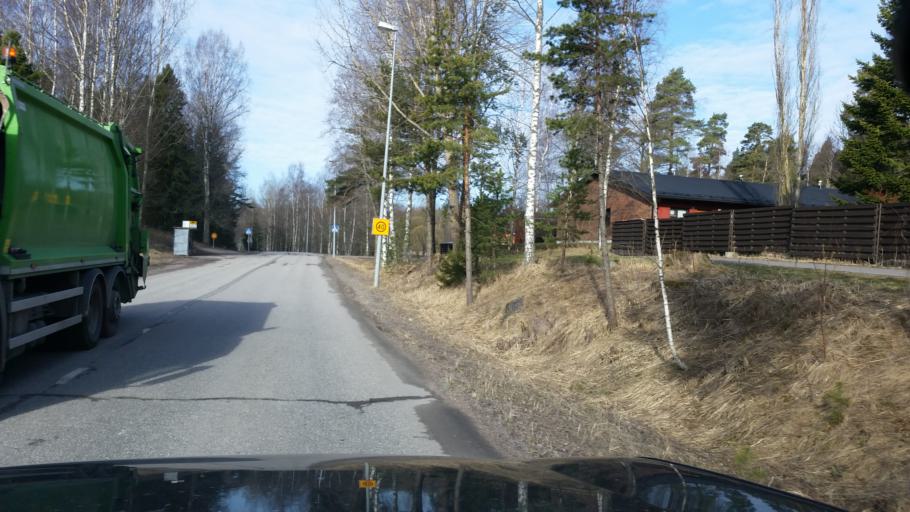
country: FI
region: Uusimaa
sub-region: Helsinki
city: Kirkkonummi
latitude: 60.0945
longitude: 24.4113
